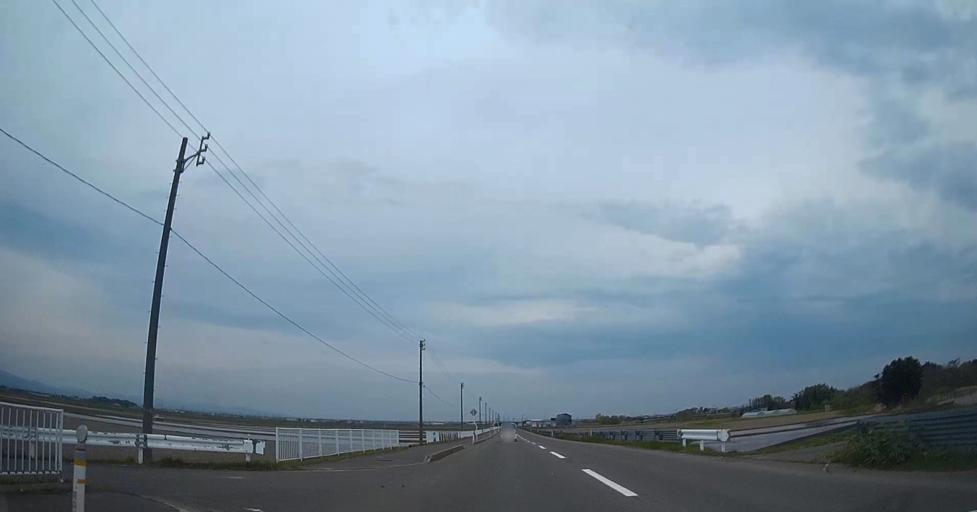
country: JP
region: Aomori
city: Goshogawara
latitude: 40.8988
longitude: 140.4739
